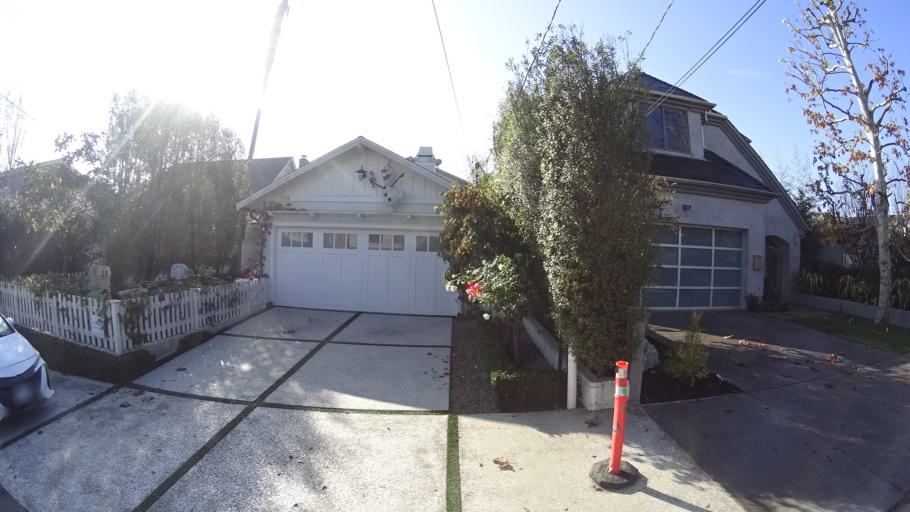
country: US
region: California
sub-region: Los Angeles County
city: Manhattan Beach
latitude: 33.8970
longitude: -118.4053
